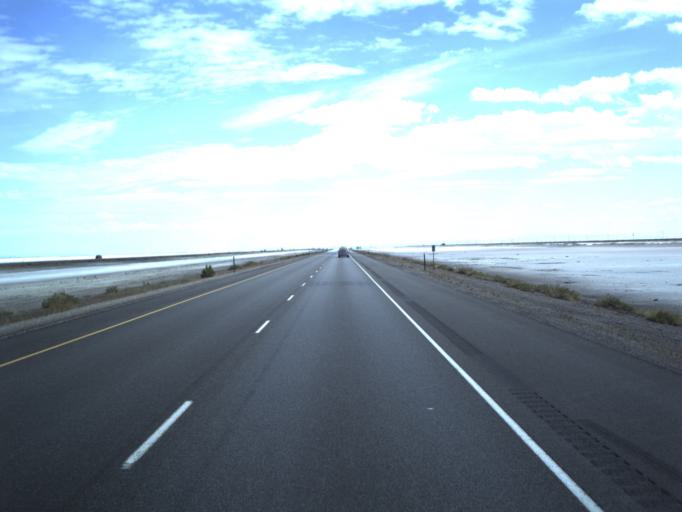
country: US
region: Utah
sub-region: Tooele County
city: Wendover
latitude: 40.7401
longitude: -113.9332
